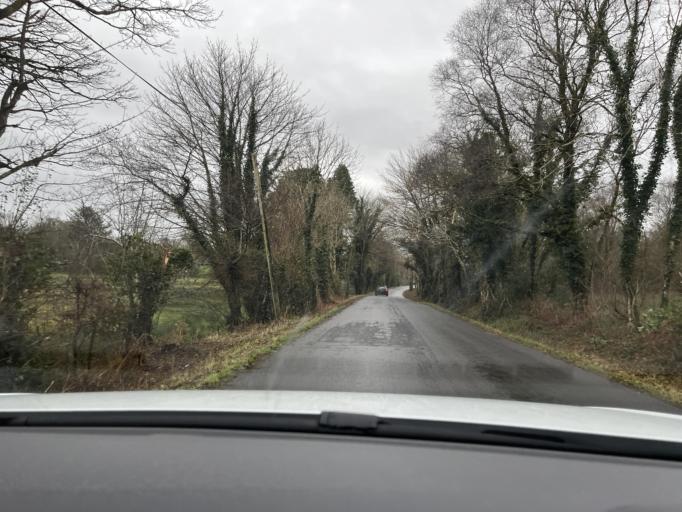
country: IE
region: Connaught
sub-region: County Leitrim
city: Manorhamilton
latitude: 54.2715
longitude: -8.2151
